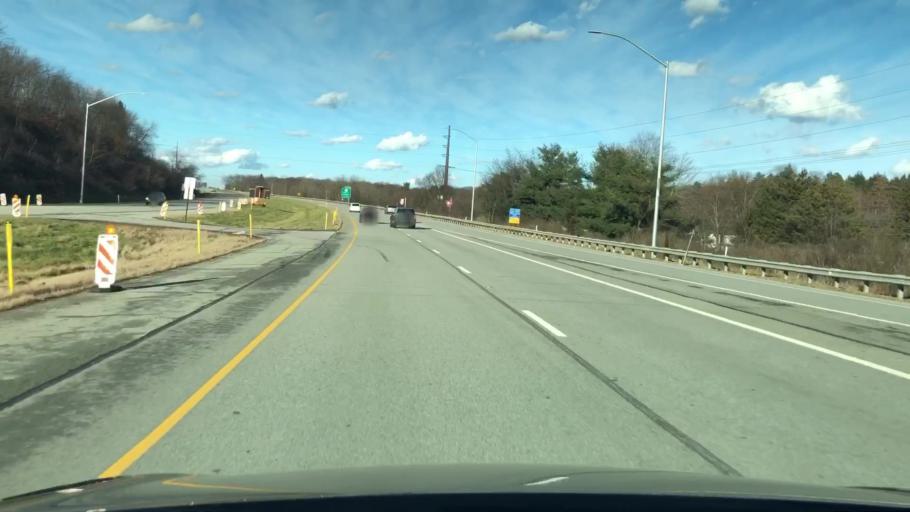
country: US
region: Pennsylvania
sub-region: Armstrong County
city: Freeport
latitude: 40.6709
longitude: -79.7140
